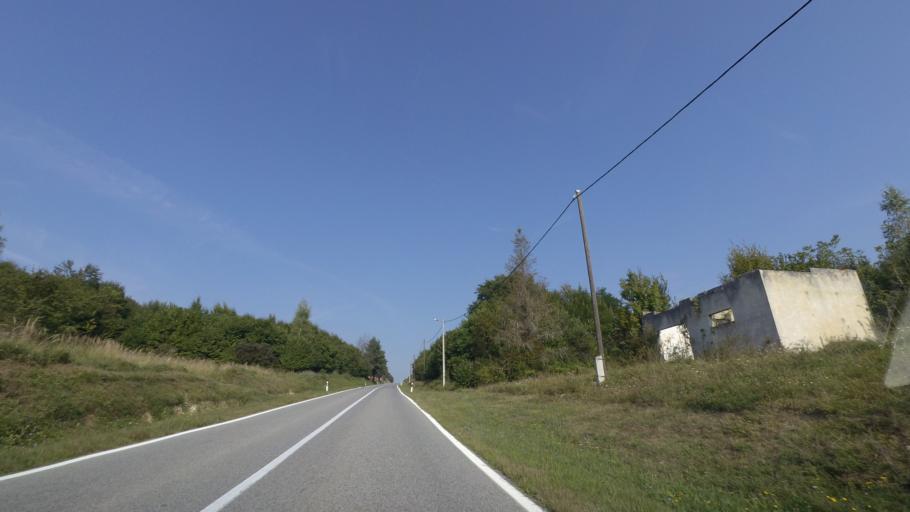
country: HR
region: Bjelovarsko-Bilogorska
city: Sirac
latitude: 45.4635
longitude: 17.4062
